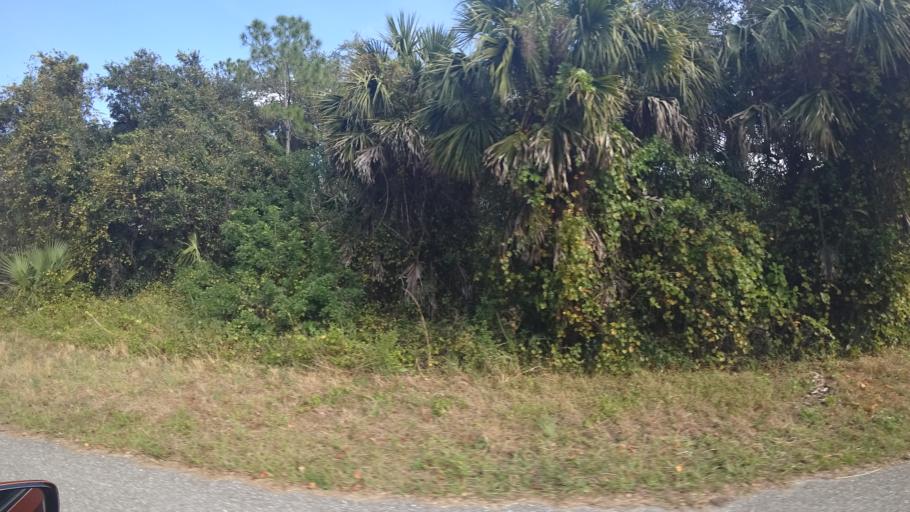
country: US
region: Florida
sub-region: Charlotte County
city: Port Charlotte
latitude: 27.0458
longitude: -82.1297
